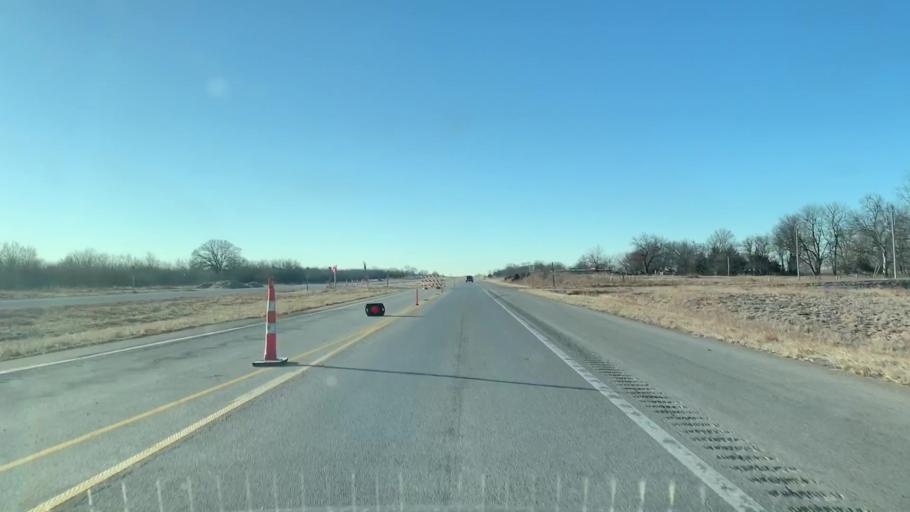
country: US
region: Kansas
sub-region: Bourbon County
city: Fort Scott
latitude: 37.7622
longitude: -94.7049
